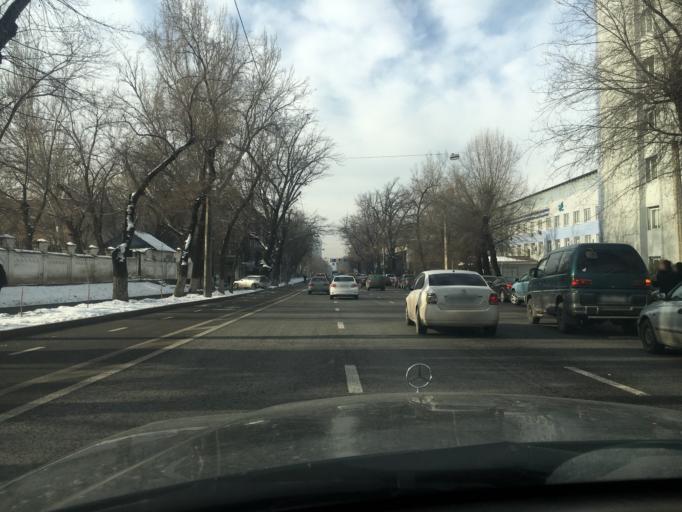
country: KZ
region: Almaty Qalasy
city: Almaty
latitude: 43.2452
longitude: 76.9300
